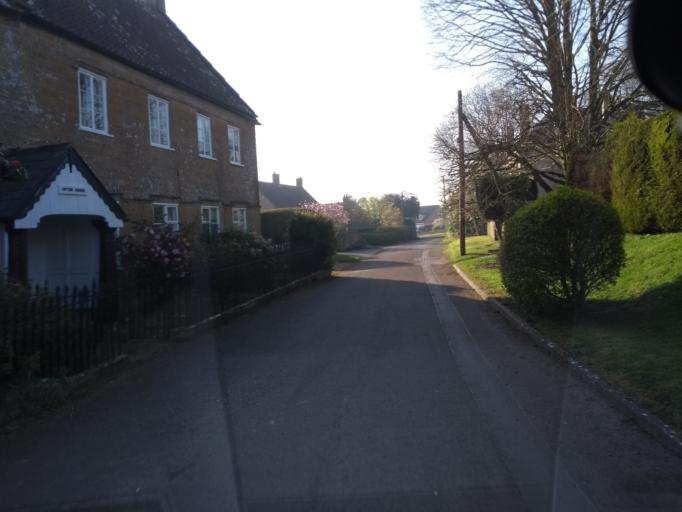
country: GB
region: England
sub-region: Somerset
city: South Petherton
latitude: 50.9345
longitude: -2.8459
